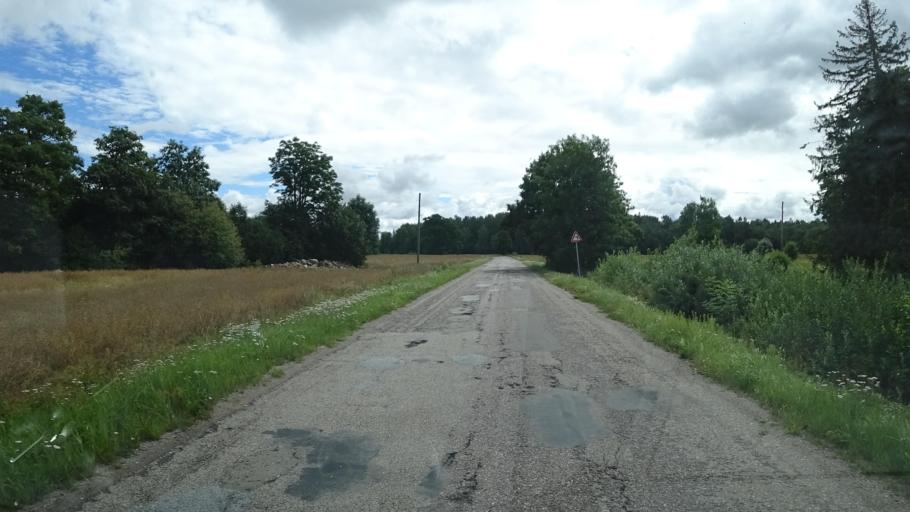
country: LV
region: Liepaja
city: Vec-Liepaja
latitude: 56.6579
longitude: 21.0880
